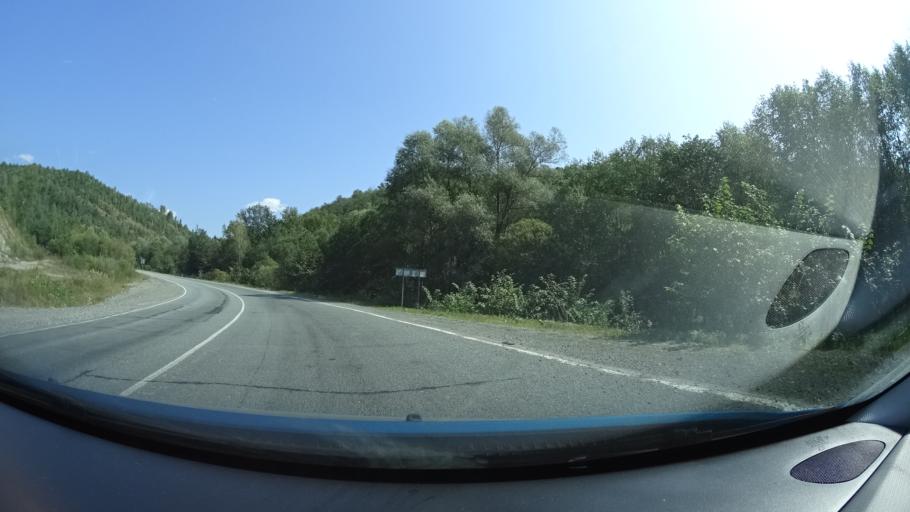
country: RU
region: Bashkortostan
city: Inzer
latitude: 54.3118
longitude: 57.1940
